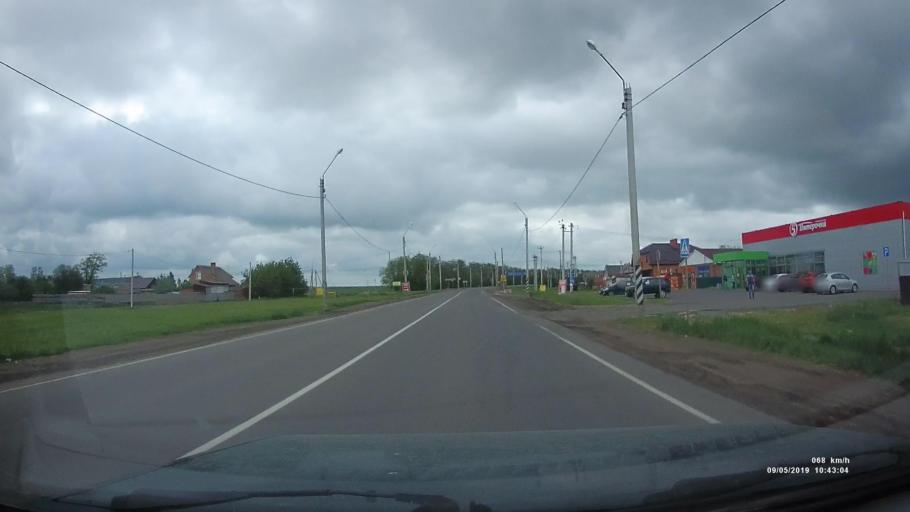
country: RU
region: Rostov
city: Peshkovo
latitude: 47.0118
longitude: 39.4039
